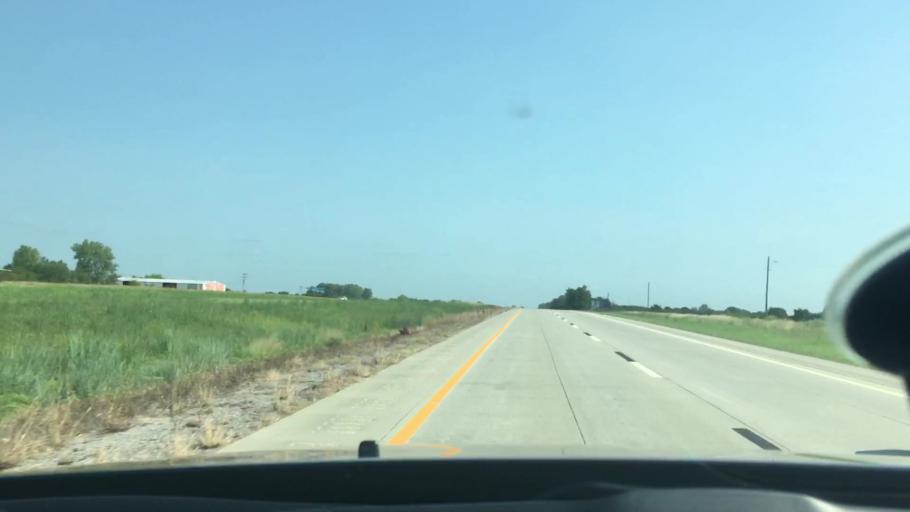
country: US
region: Oklahoma
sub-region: Atoka County
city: Atoka
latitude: 34.1941
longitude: -96.2411
